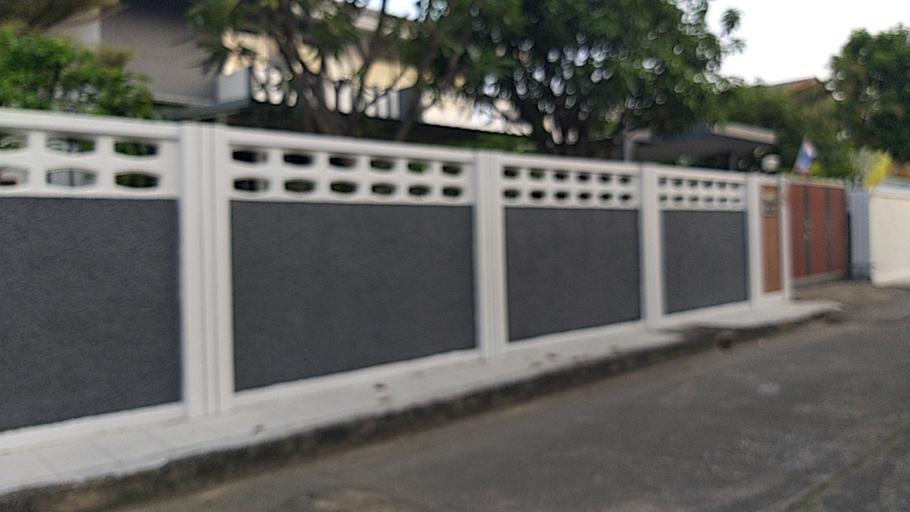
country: TH
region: Bangkok
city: Lat Phrao
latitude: 13.8283
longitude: 100.6076
